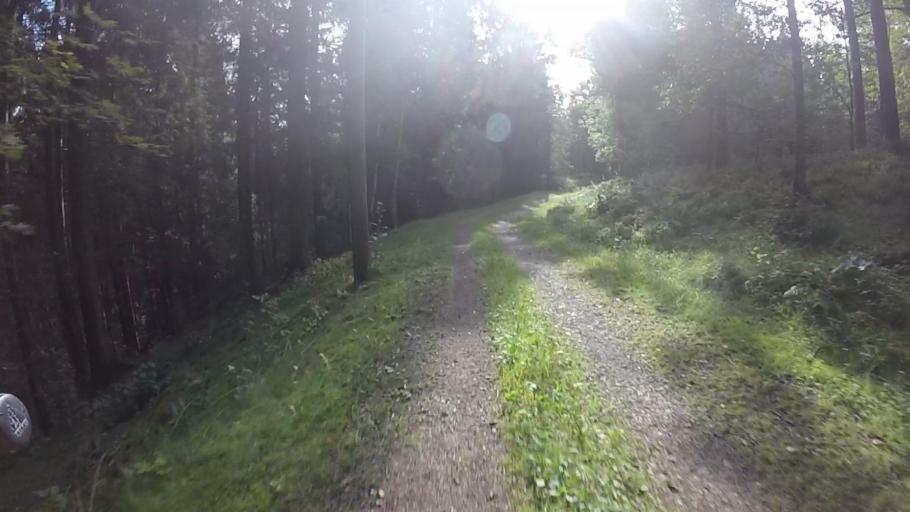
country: SE
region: Vaestra Goetaland
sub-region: Trollhattan
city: Trollhattan
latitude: 58.2546
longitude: 12.2613
